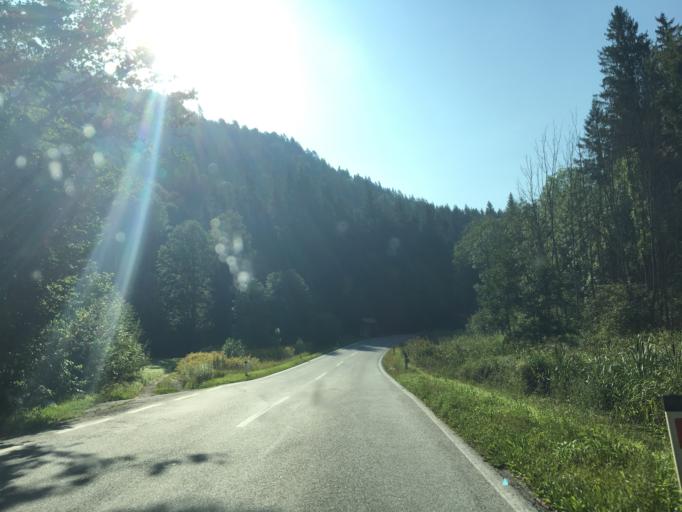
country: AT
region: Carinthia
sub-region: Politischer Bezirk Sankt Veit an der Glan
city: Bruckl
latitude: 46.7179
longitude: 14.5595
